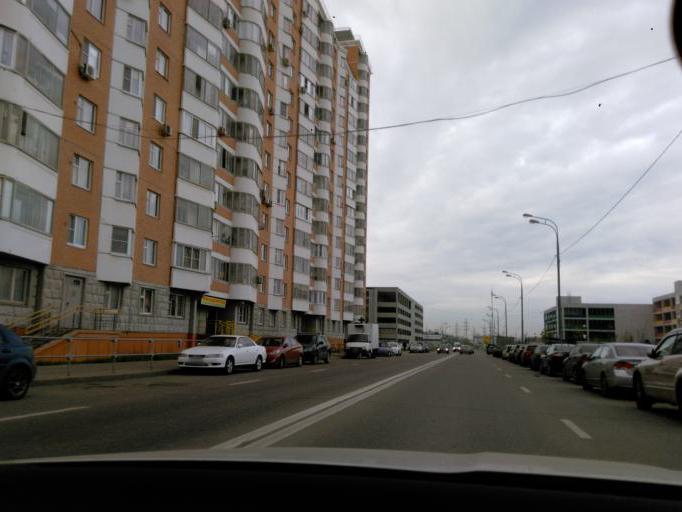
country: RU
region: Moscow
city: Severnyy
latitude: 55.9225
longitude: 37.5405
